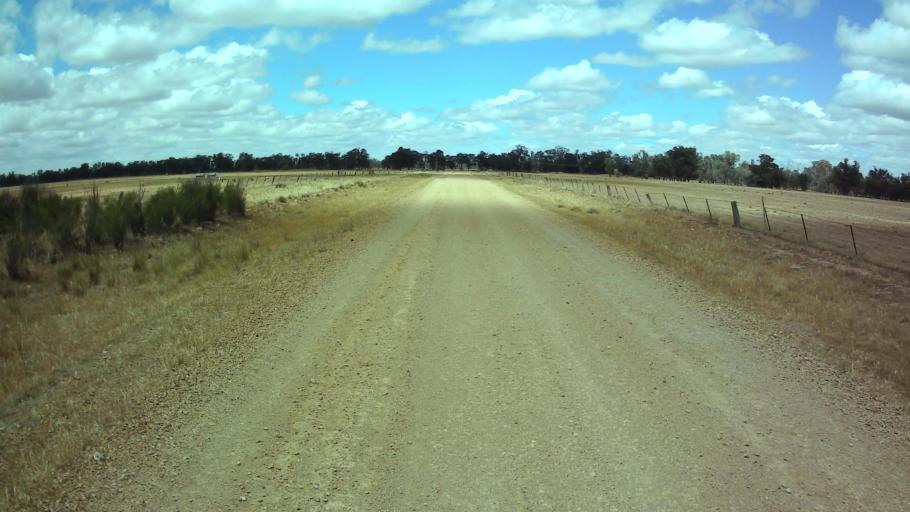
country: AU
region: New South Wales
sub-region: Weddin
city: Grenfell
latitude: -34.0263
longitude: 147.9135
